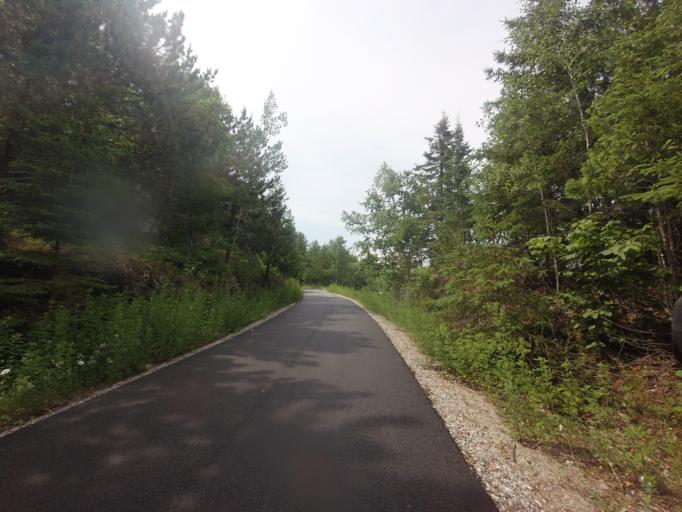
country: CA
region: Quebec
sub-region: Outaouais
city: Maniwaki
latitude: 46.2103
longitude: -76.0394
